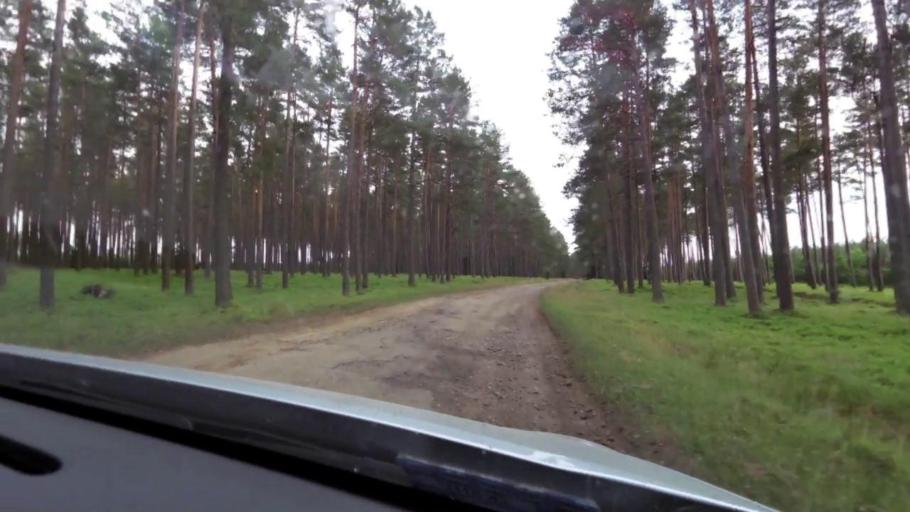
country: PL
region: Pomeranian Voivodeship
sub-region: Powiat bytowski
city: Trzebielino
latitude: 54.2086
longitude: 17.0060
